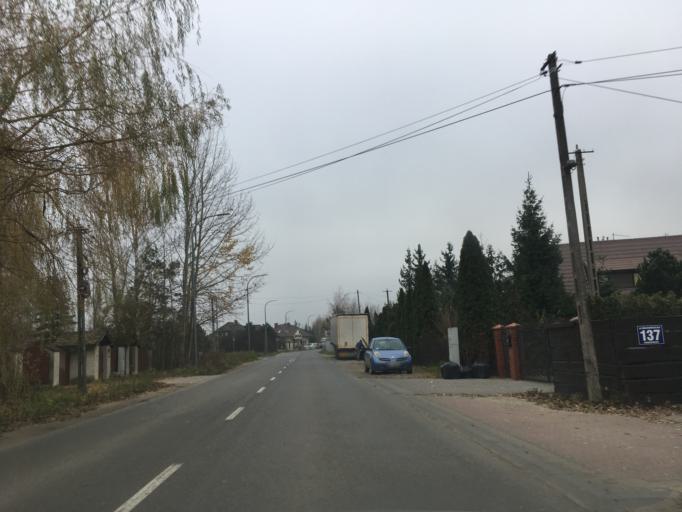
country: PL
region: Masovian Voivodeship
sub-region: Powiat piaseczynski
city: Lesznowola
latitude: 52.0731
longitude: 20.9665
